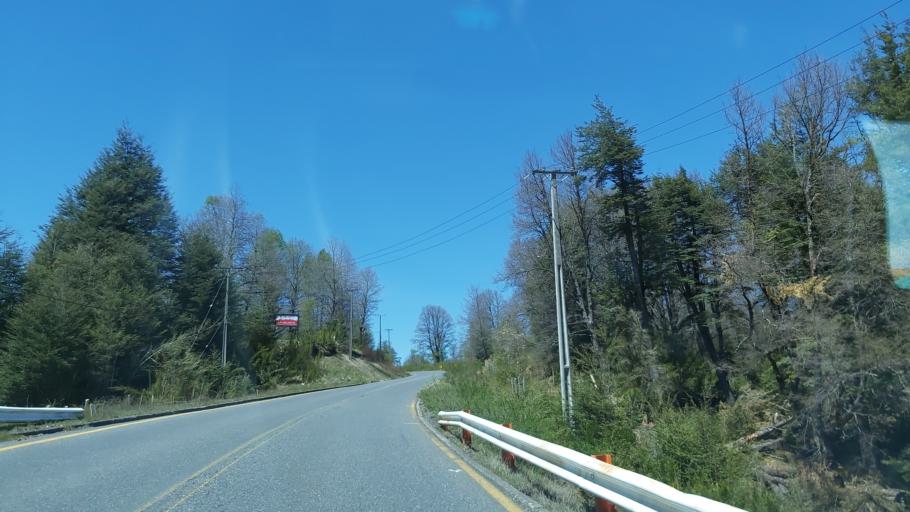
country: CL
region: Araucania
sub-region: Provincia de Cautin
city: Vilcun
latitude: -38.4625
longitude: -71.6274
